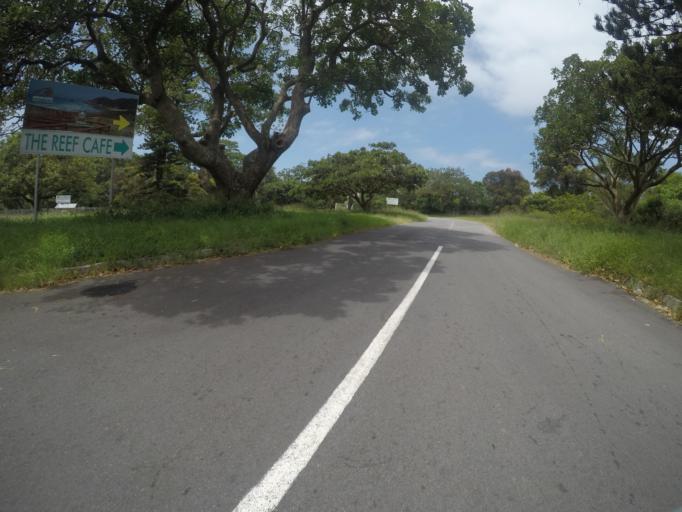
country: ZA
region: Eastern Cape
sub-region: Buffalo City Metropolitan Municipality
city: East London
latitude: -32.9934
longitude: 27.9340
